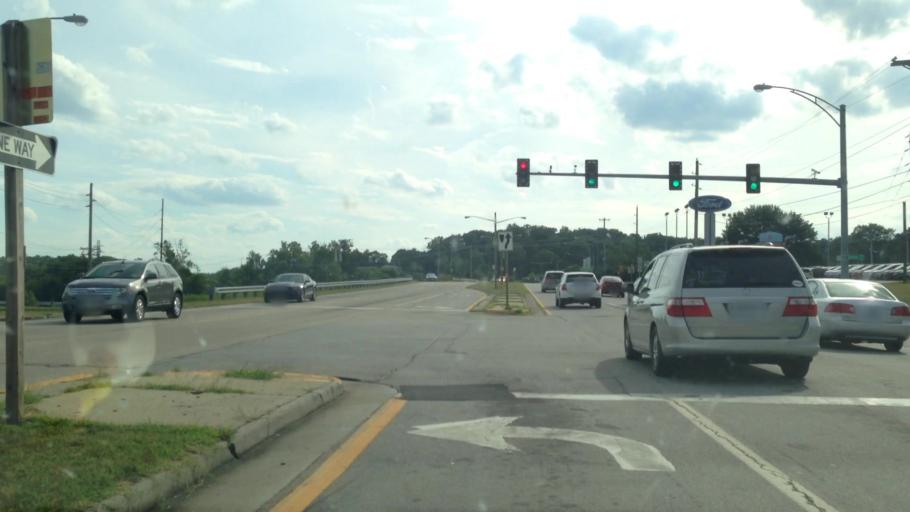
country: US
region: Virginia
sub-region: City of Danville
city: Danville
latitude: 36.5822
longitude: -79.4301
